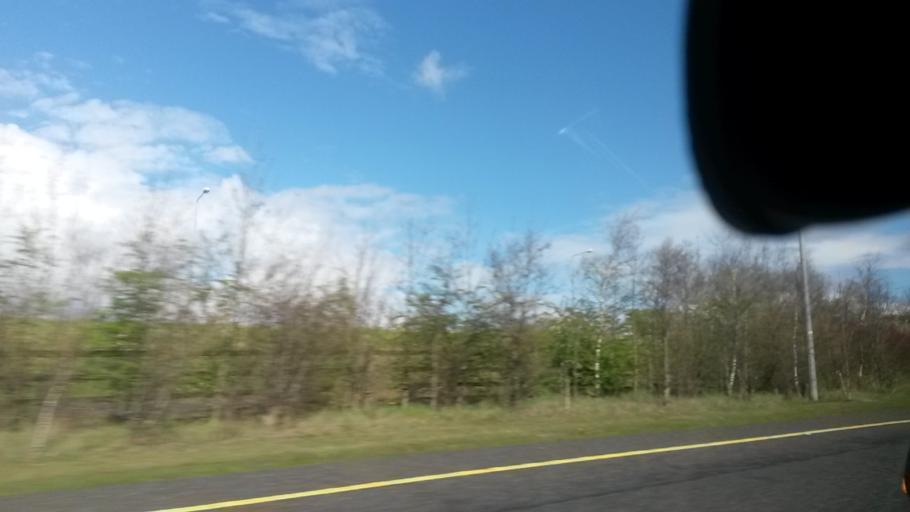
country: IE
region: Leinster
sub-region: Kildare
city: Monasterevin
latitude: 53.1440
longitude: -7.0227
